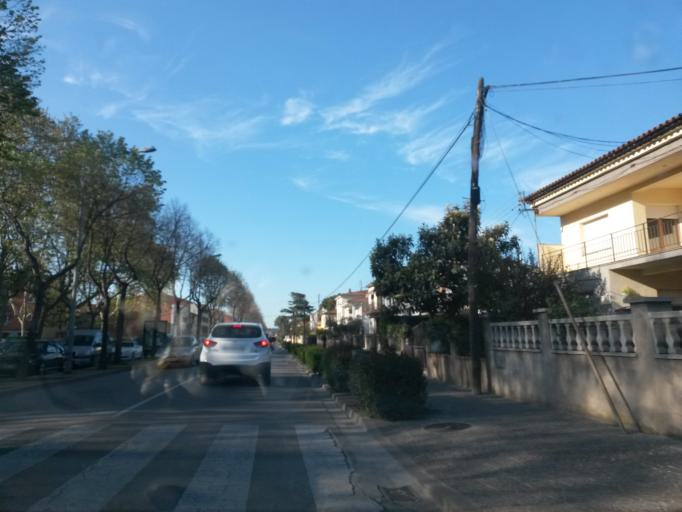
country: ES
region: Catalonia
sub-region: Provincia de Girona
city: Sarria de Ter
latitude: 42.0045
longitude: 2.8248
